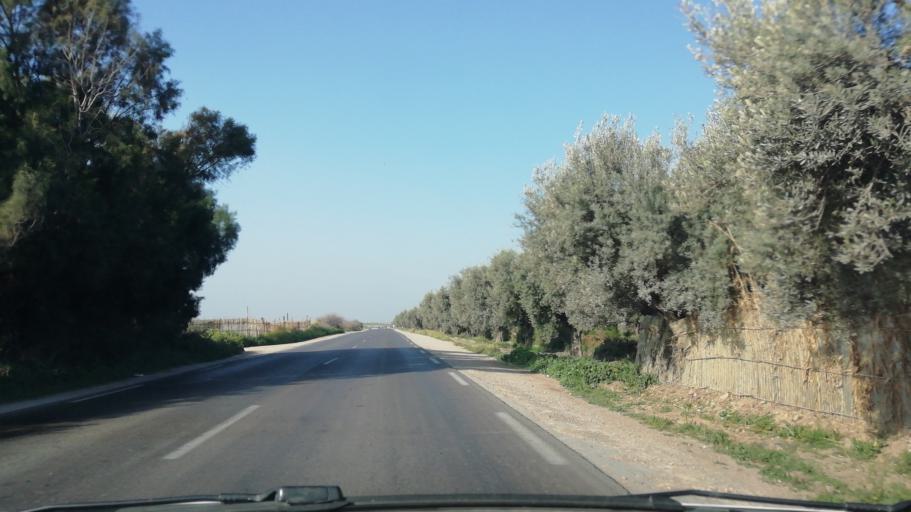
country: DZ
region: Mostaganem
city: Mostaganem
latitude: 35.7461
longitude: 0.1544
